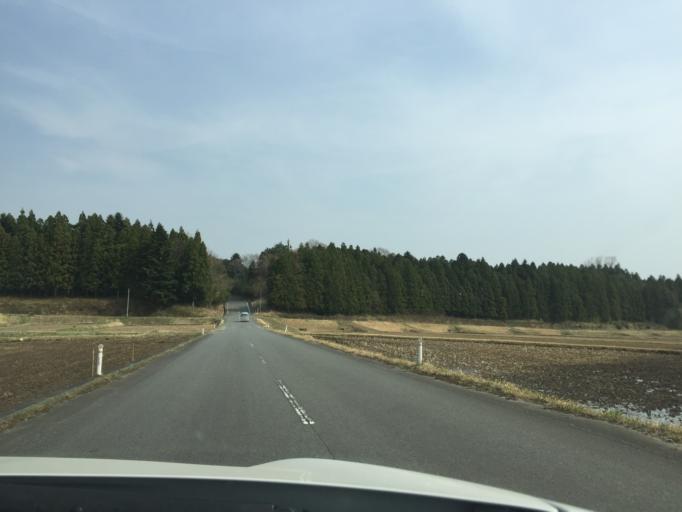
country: JP
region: Fukushima
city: Iwaki
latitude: 37.0276
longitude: 140.7472
